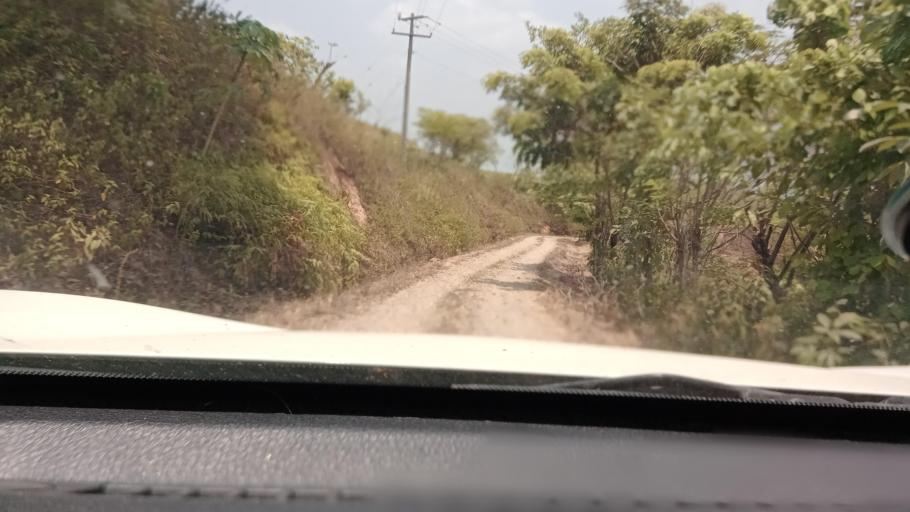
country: MX
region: Tabasco
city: Chontalpa
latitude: 17.5548
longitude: -93.7337
